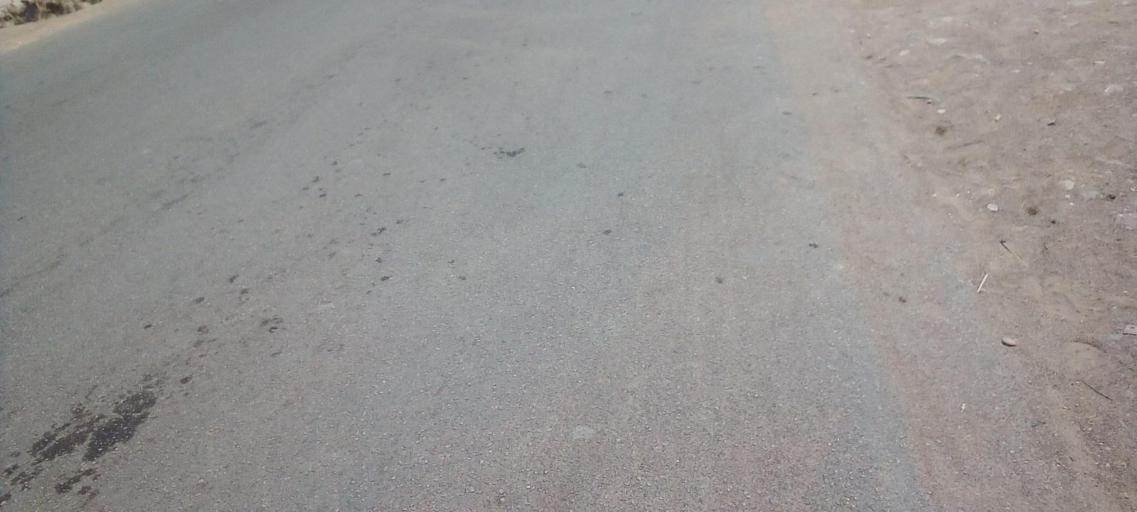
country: ZM
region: Lusaka
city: Lusaka
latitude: -15.4462
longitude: 28.2460
